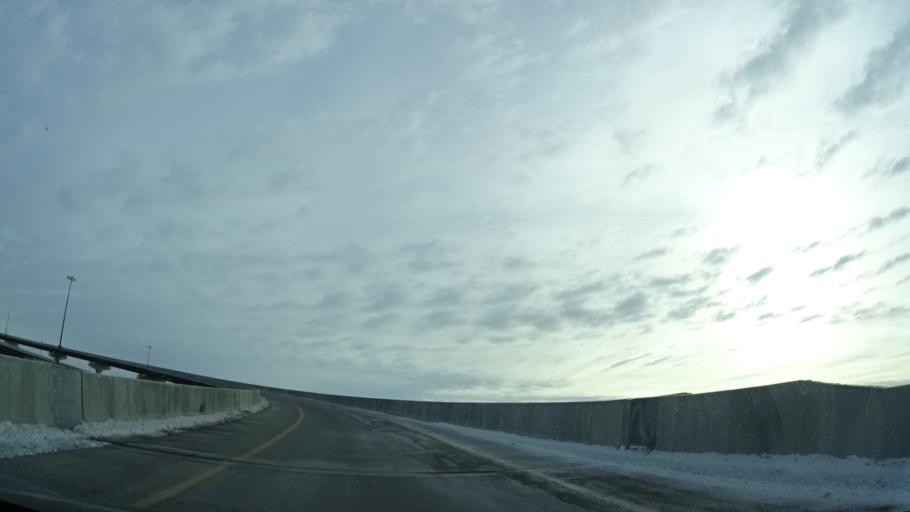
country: US
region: Nebraska
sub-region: Douglas County
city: Omaha
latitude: 41.2312
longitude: -95.8994
